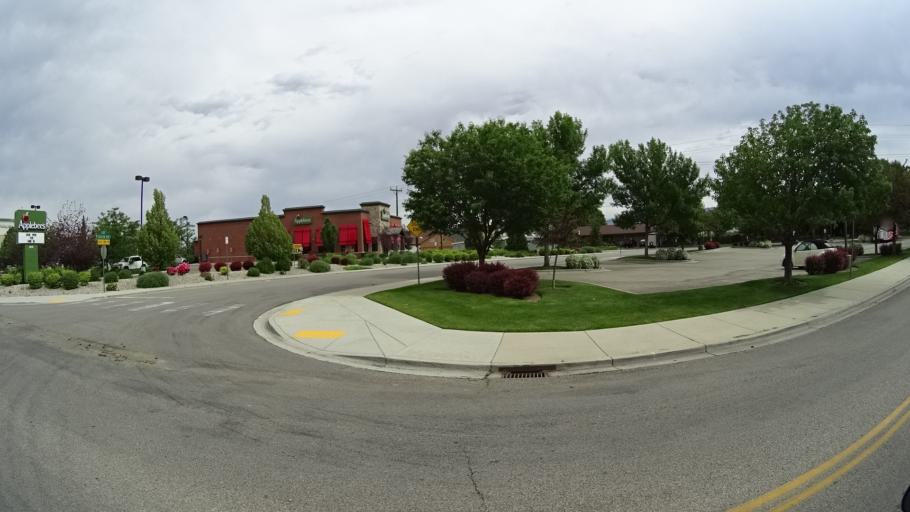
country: US
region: Idaho
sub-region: Ada County
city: Boise
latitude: 43.5735
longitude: -116.2158
